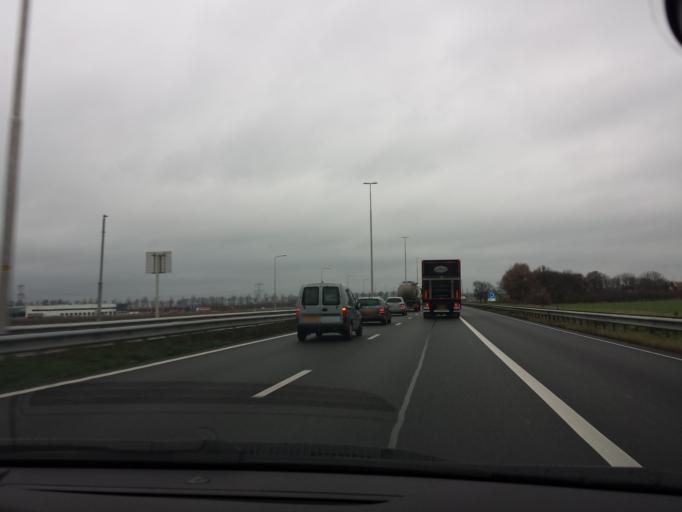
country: NL
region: Limburg
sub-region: Gemeente Sittard-Geleen
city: Born
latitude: 51.0646
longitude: 5.8247
